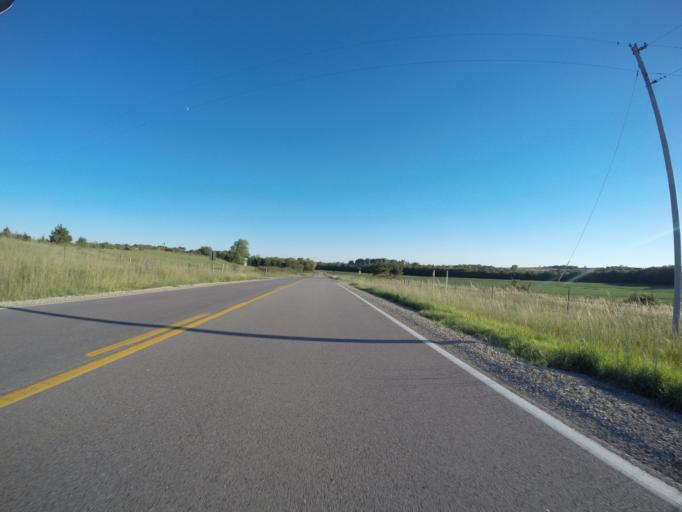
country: US
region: Kansas
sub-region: Riley County
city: Fort Riley North
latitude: 39.2625
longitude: -96.7752
